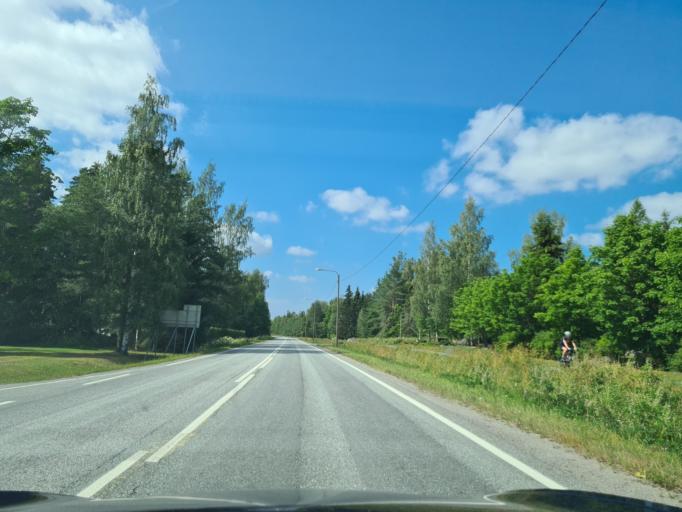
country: FI
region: Ostrobothnia
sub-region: Vaasa
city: Vaasa
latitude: 63.1933
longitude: 21.5577
